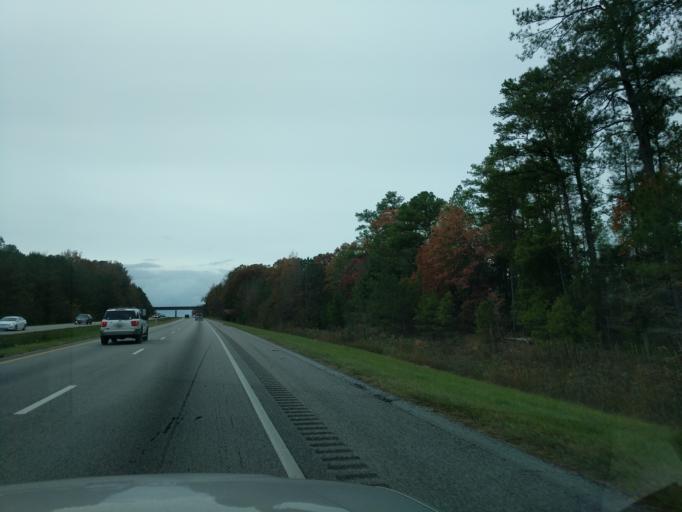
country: US
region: South Carolina
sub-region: Laurens County
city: Joanna
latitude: 34.4774
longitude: -81.8176
